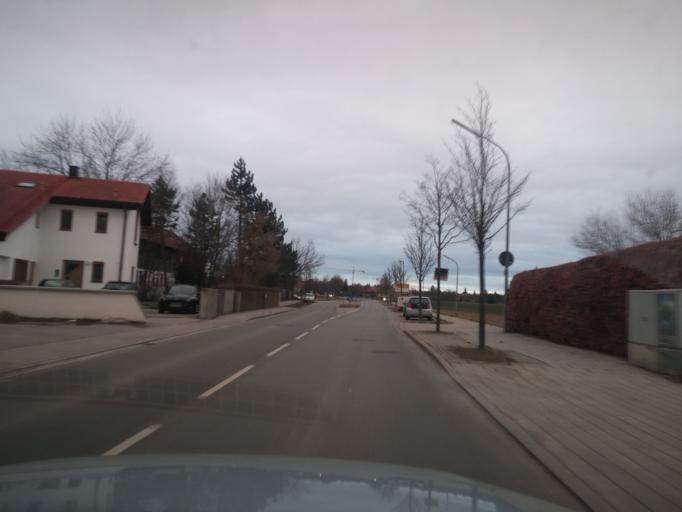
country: DE
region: Bavaria
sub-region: Upper Bavaria
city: Haar
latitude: 48.1266
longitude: 11.7411
